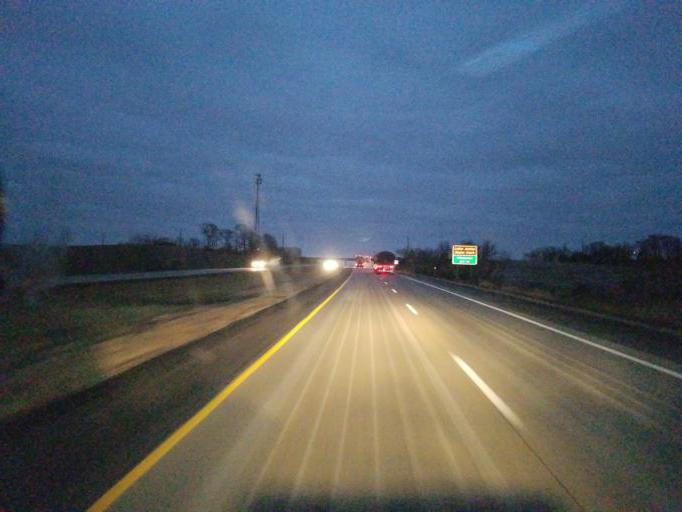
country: US
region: Iowa
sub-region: Cass County
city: Atlantic
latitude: 41.4962
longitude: -94.7825
